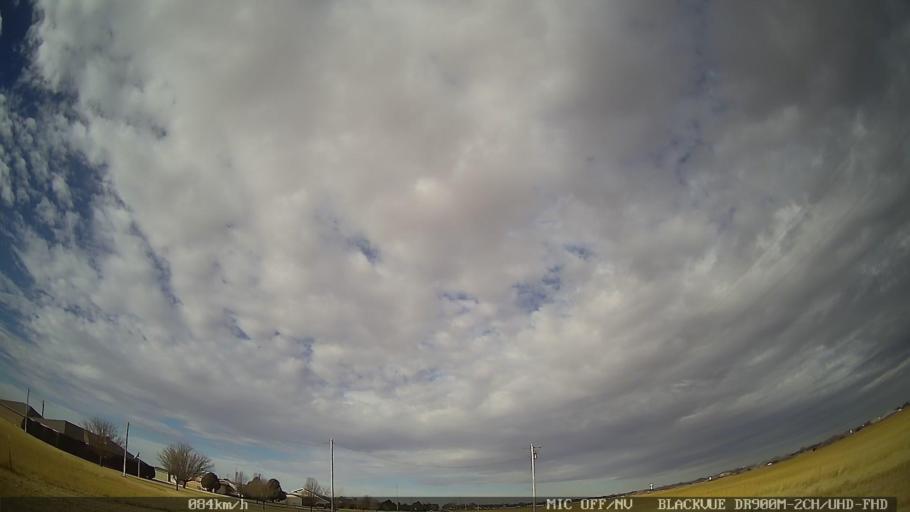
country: US
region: New Mexico
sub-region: Curry County
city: Clovis
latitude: 34.4194
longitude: -103.1550
